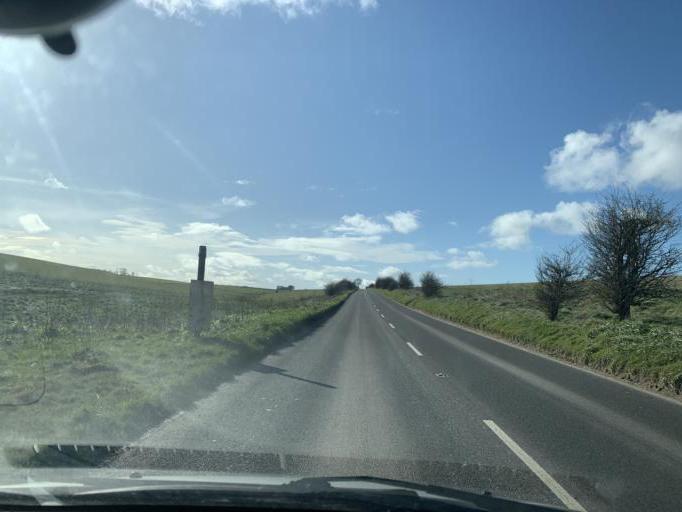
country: GB
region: England
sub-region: Wiltshire
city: Shrewton
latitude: 51.1911
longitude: -1.9620
